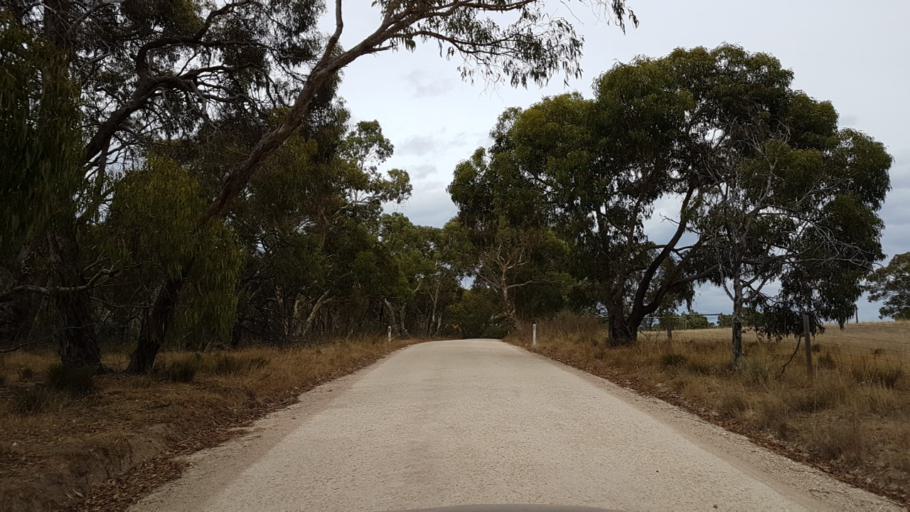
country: AU
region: South Australia
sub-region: Adelaide Hills
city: Birdwood
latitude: -34.7864
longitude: 138.9764
